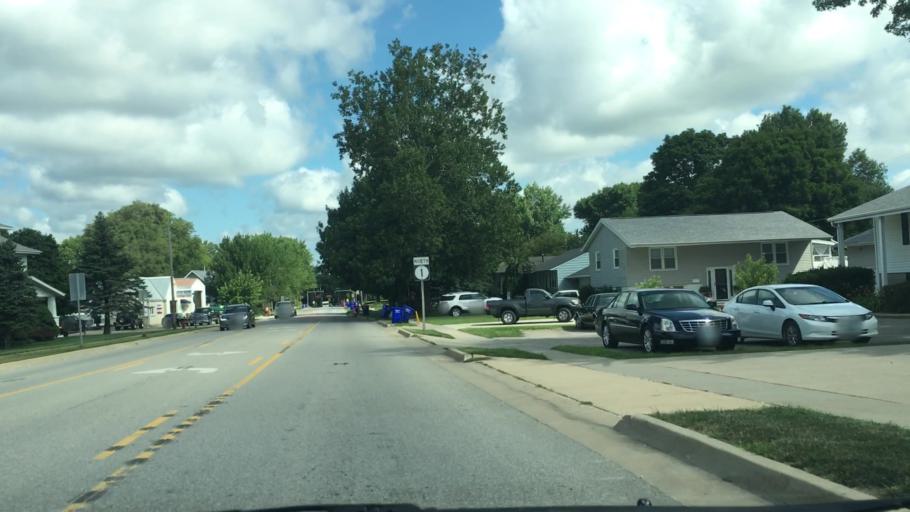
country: US
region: Iowa
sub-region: Johnson County
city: Solon
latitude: 41.8023
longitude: -91.4917
